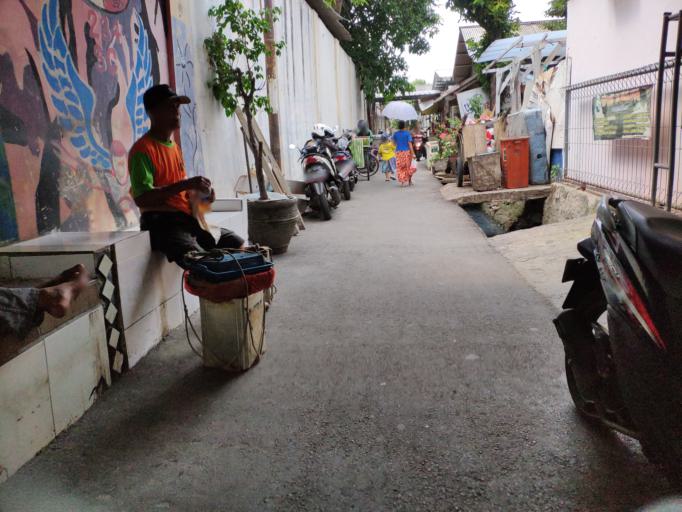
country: ID
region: Jakarta Raya
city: Jakarta
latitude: -6.1971
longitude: 106.8696
